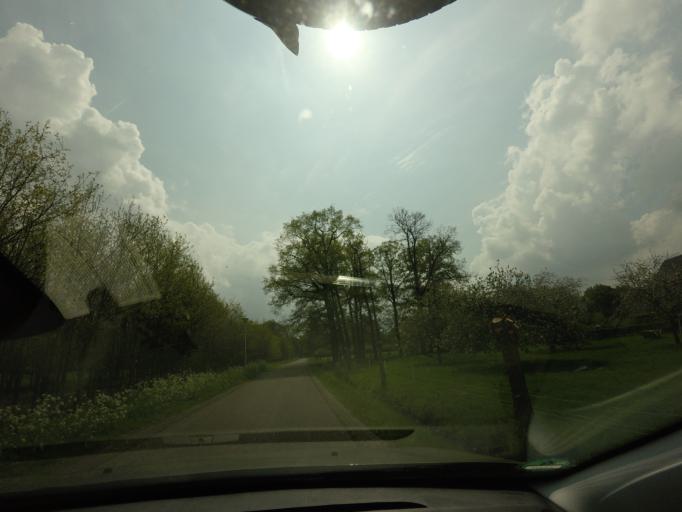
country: NL
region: Overijssel
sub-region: Gemeente Haaksbergen
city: Haaksbergen
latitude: 52.1780
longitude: 6.8095
